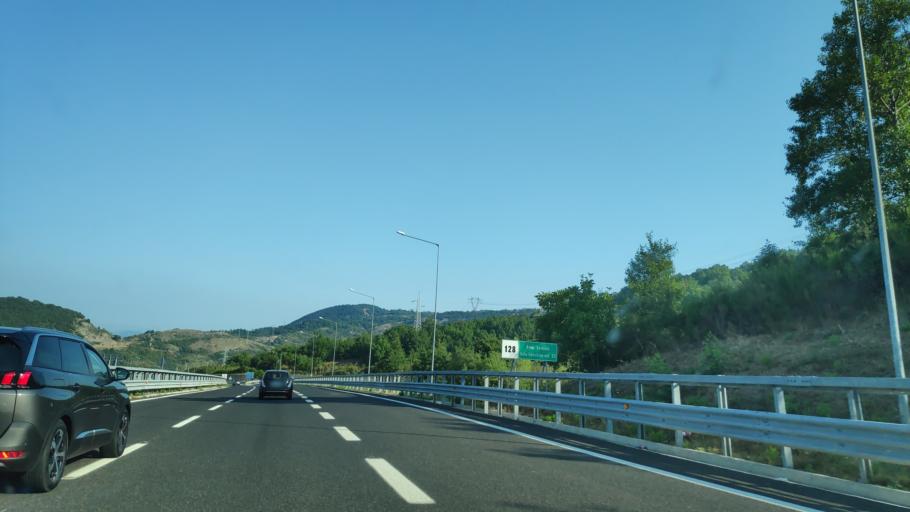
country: IT
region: Basilicate
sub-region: Provincia di Potenza
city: Lagonegro
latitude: 40.1507
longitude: 15.7502
